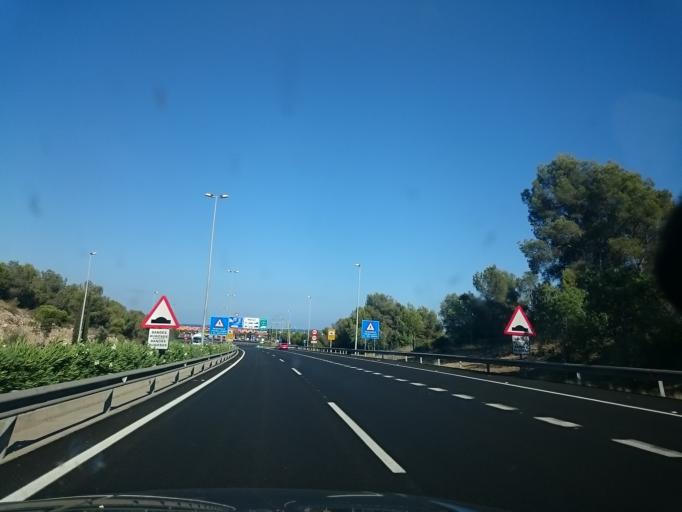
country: ES
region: Catalonia
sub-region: Provincia de Tarragona
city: Cunit
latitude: 41.2087
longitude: 1.6463
